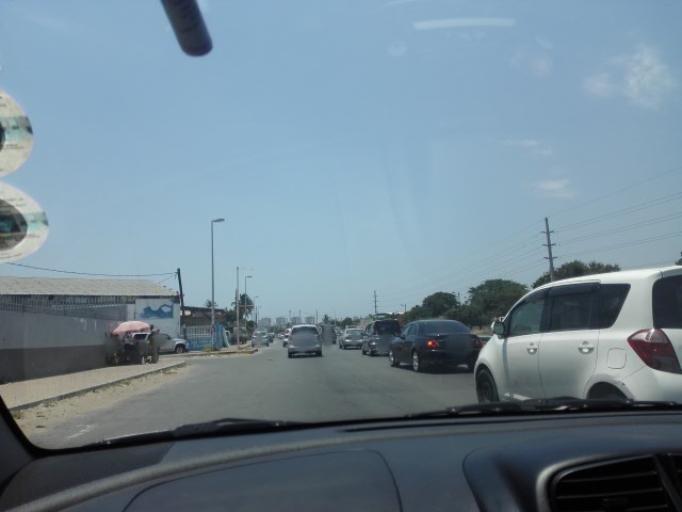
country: MZ
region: Maputo City
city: Maputo
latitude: -25.9421
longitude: 32.5715
